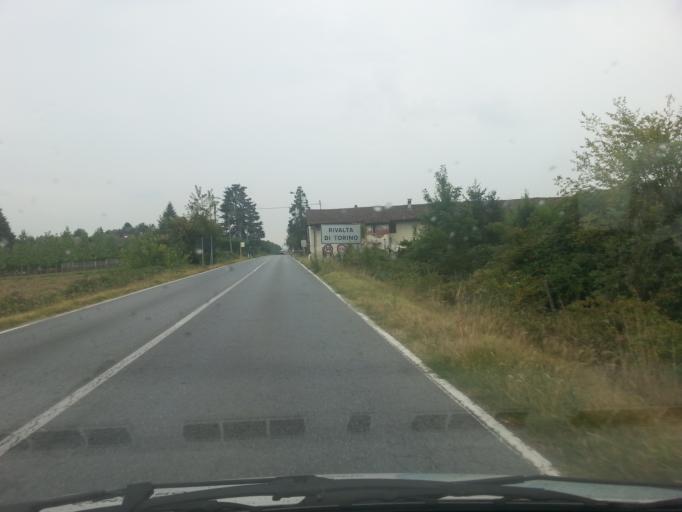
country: IT
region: Piedmont
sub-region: Provincia di Torino
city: Rivalta di Torino
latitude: 45.0444
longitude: 7.5220
